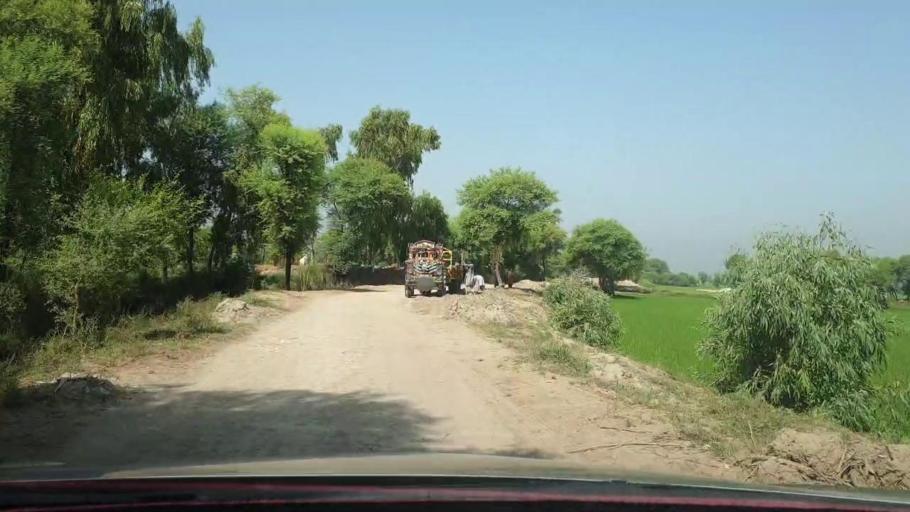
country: PK
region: Sindh
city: Warah
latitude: 27.4551
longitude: 67.8711
